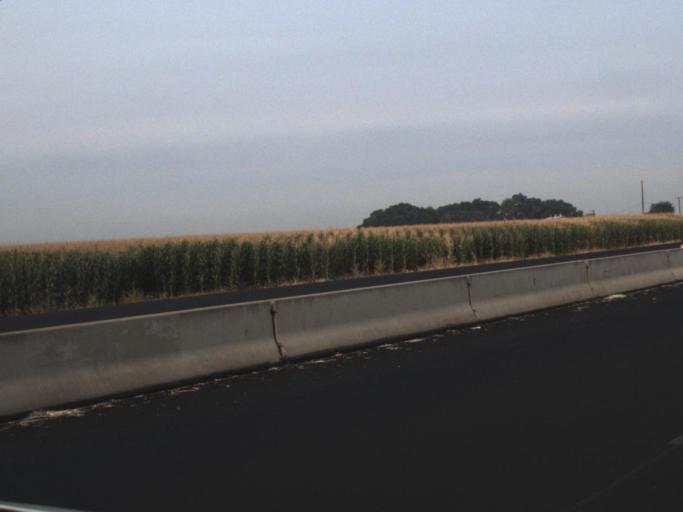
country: US
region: Washington
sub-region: Yakima County
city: Toppenish
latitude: 46.3851
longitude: -120.3491
